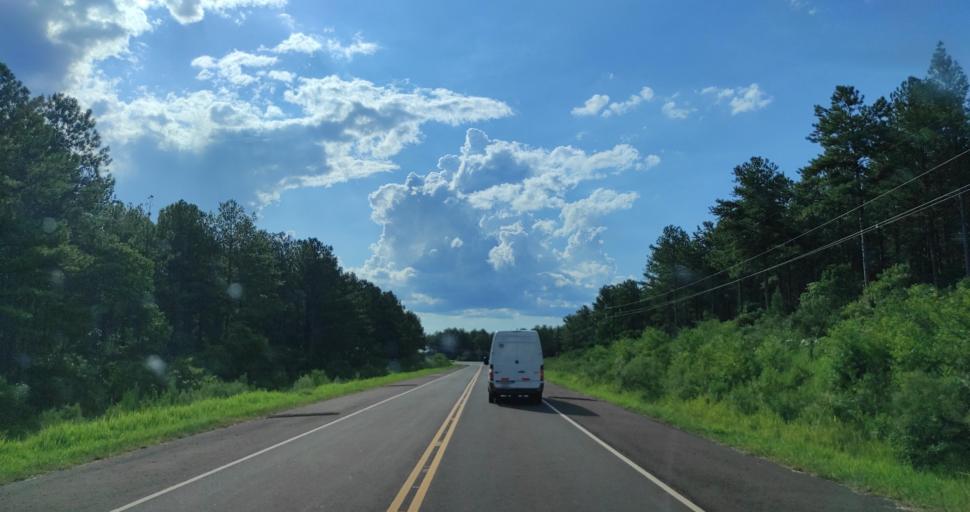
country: AR
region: Misiones
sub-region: Departamento de San Pedro
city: San Pedro
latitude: -26.3491
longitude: -53.9697
